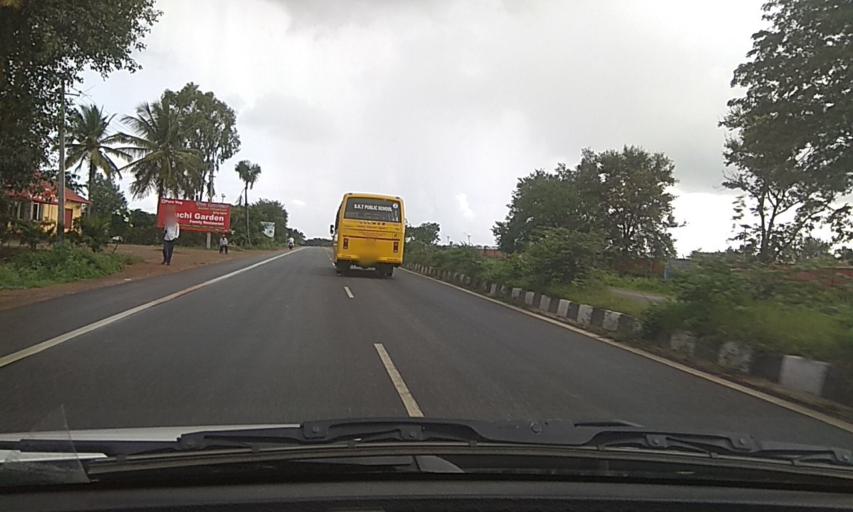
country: IN
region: Karnataka
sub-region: Mysore
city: Mysore
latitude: 12.2347
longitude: 76.6622
